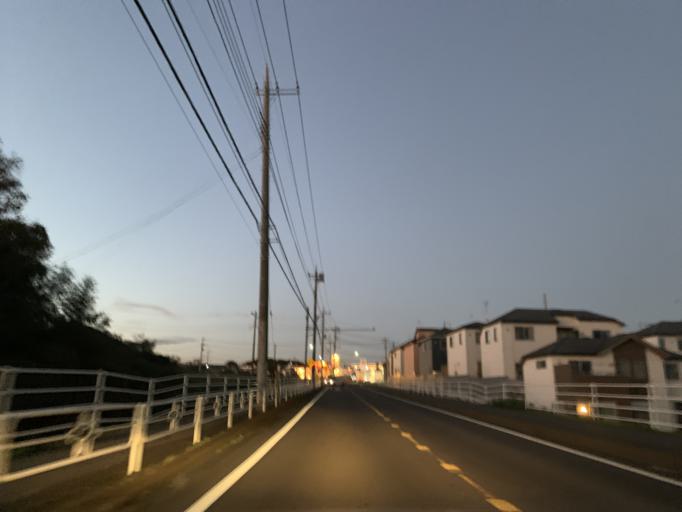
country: JP
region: Chiba
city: Nagareyama
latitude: 35.8927
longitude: 139.9006
